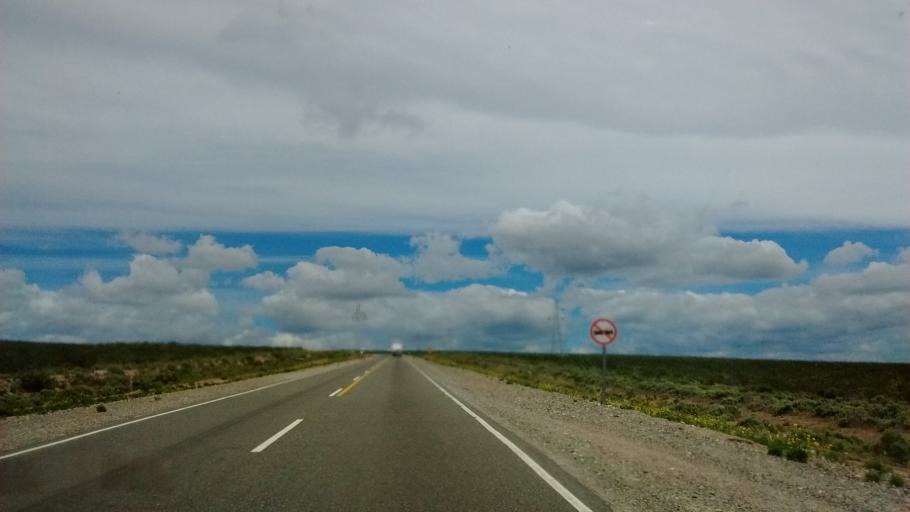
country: AR
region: Neuquen
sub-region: Departamento de Picun Leufu
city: Picun Leufu
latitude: -39.7319
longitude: -69.5801
